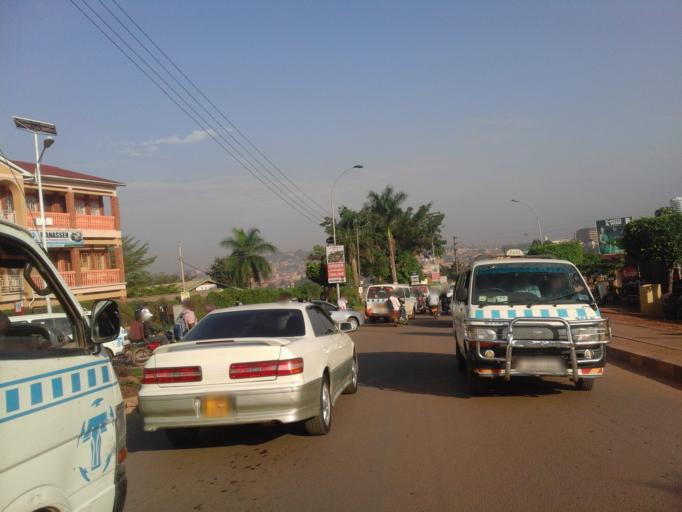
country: UG
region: Central Region
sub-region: Kampala District
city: Kampala
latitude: 0.3038
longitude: 32.5853
